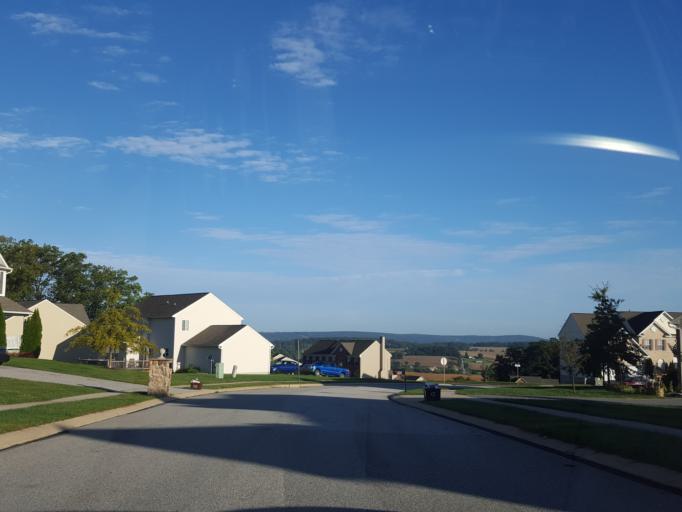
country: US
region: Pennsylvania
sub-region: York County
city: Windsor
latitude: 39.9460
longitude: -76.6083
